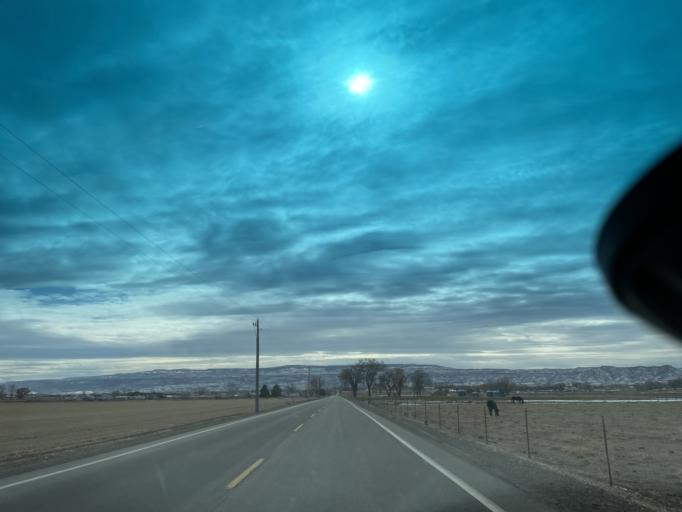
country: US
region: Colorado
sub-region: Mesa County
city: Loma
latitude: 39.2432
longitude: -108.8129
